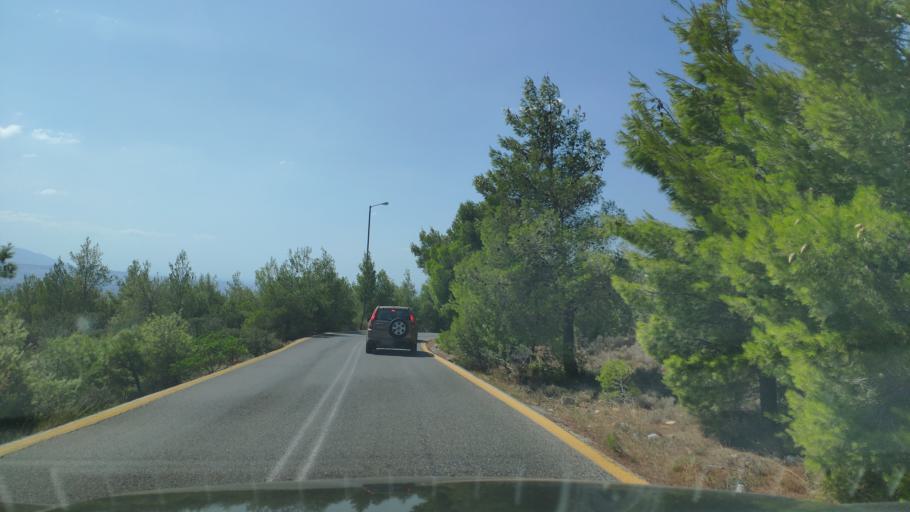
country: GR
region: Attica
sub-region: Nomarchia Anatolikis Attikis
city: Thrakomakedones
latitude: 38.1323
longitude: 23.7414
